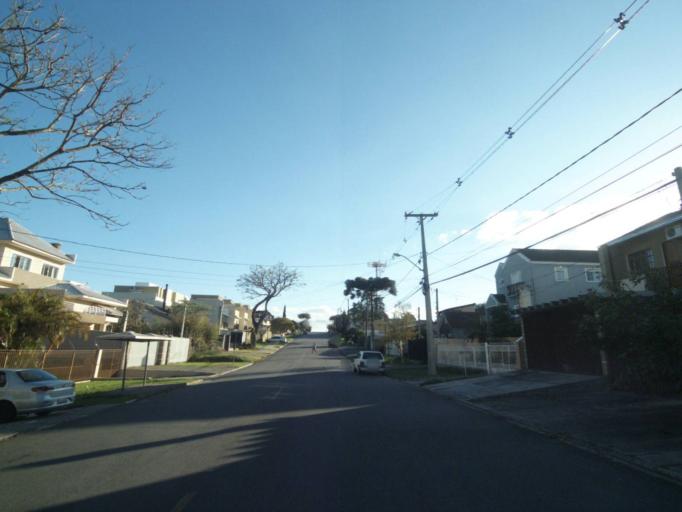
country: BR
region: Parana
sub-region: Curitiba
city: Curitiba
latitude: -25.3877
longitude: -49.2472
